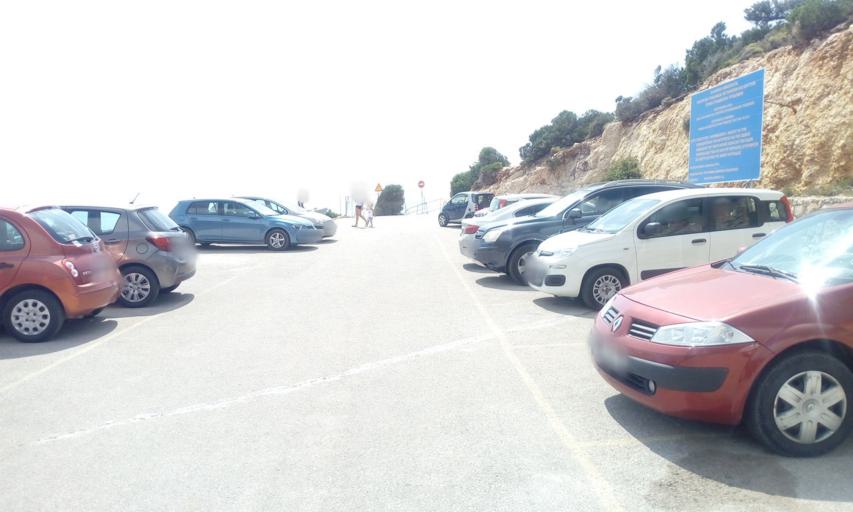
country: GR
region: Ionian Islands
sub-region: Lefkada
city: Nidri
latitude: 38.6030
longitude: 20.5491
